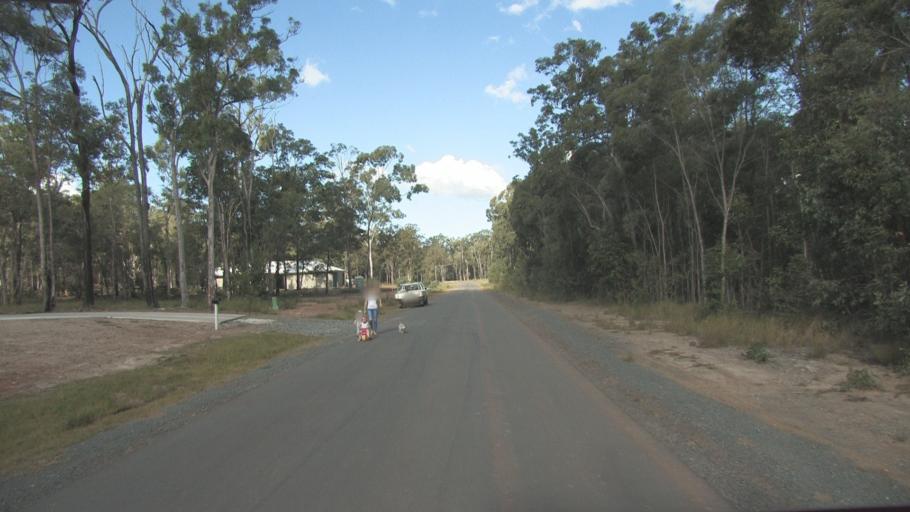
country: AU
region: Queensland
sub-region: Gold Coast
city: Yatala
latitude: -27.6669
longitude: 153.2514
